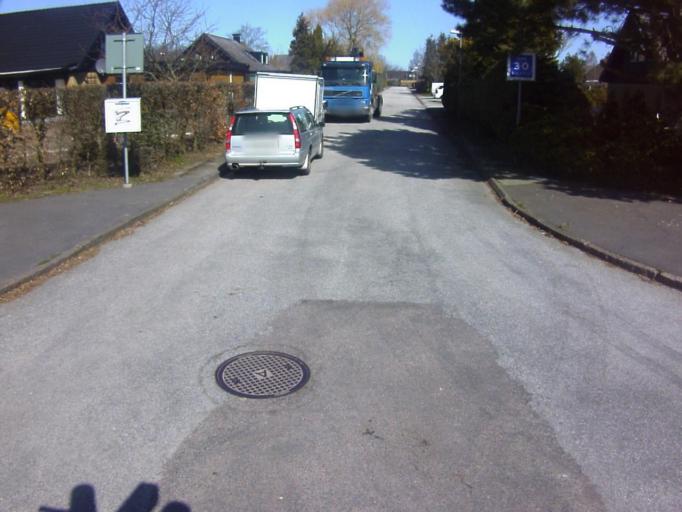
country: SE
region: Skane
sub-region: Kavlinge Kommun
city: Kaevlinge
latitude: 55.7921
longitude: 13.0874
